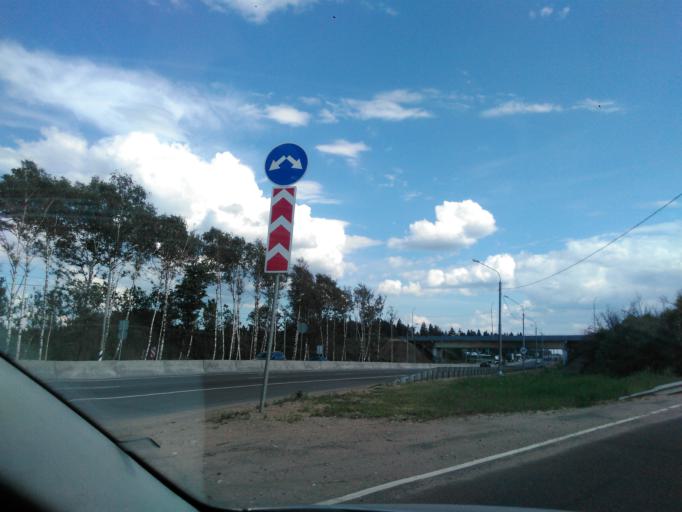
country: RU
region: Moskovskaya
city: Peshki
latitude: 56.1520
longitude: 37.0336
